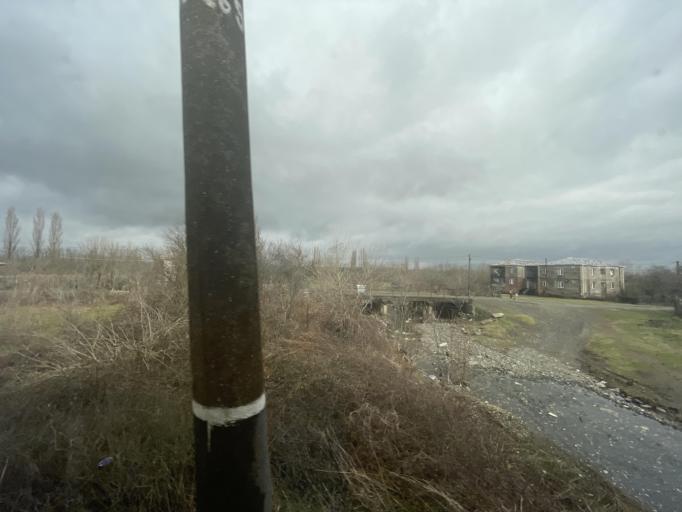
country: GE
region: Guria
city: Lanchkhuti
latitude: 42.0955
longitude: 42.0274
